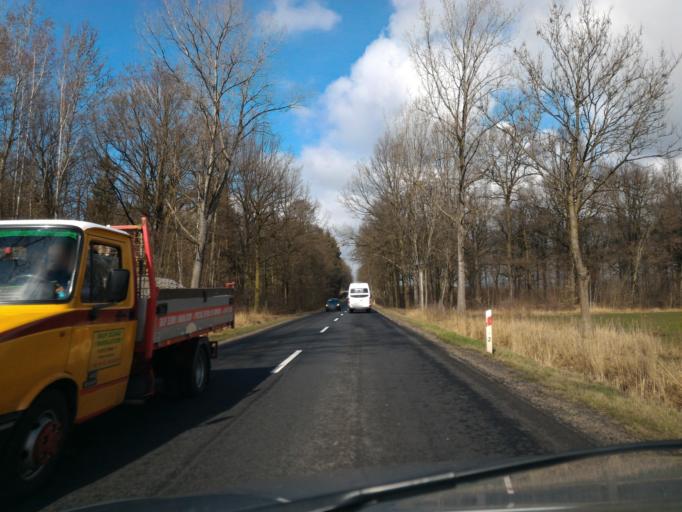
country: PL
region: Lower Silesian Voivodeship
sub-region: Powiat zgorzelecki
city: Sulikow
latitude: 51.0665
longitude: 15.0335
